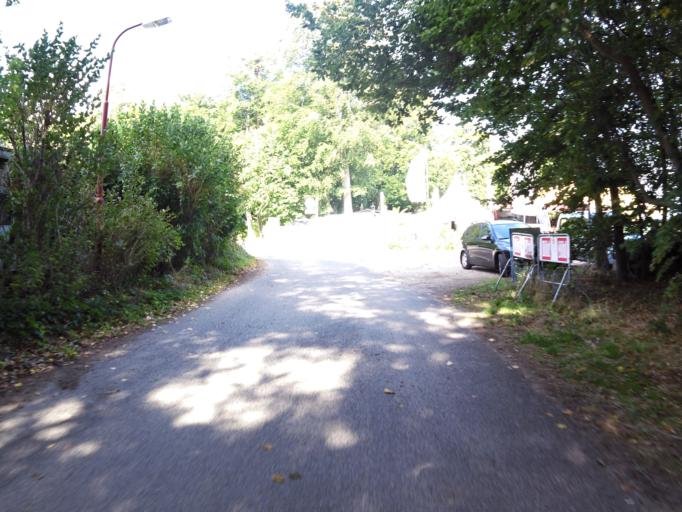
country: DE
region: Mecklenburg-Vorpommern
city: Seebad Bansin
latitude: 53.9955
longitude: 14.1078
